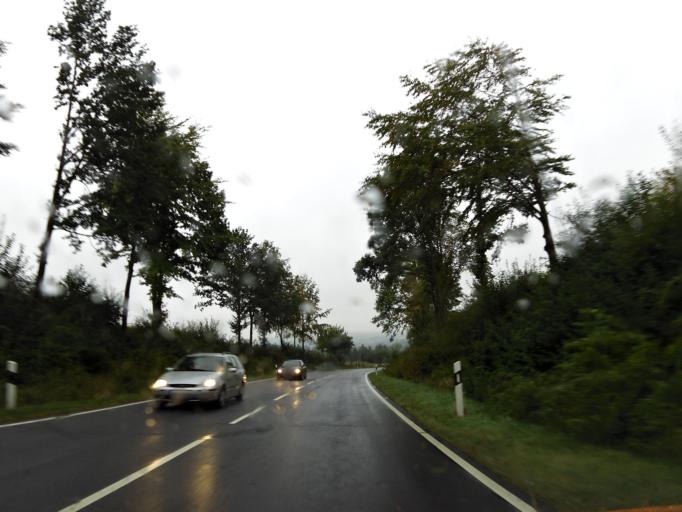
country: DE
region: Lower Saxony
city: Bad Sachsa
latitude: 51.5866
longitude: 10.5294
